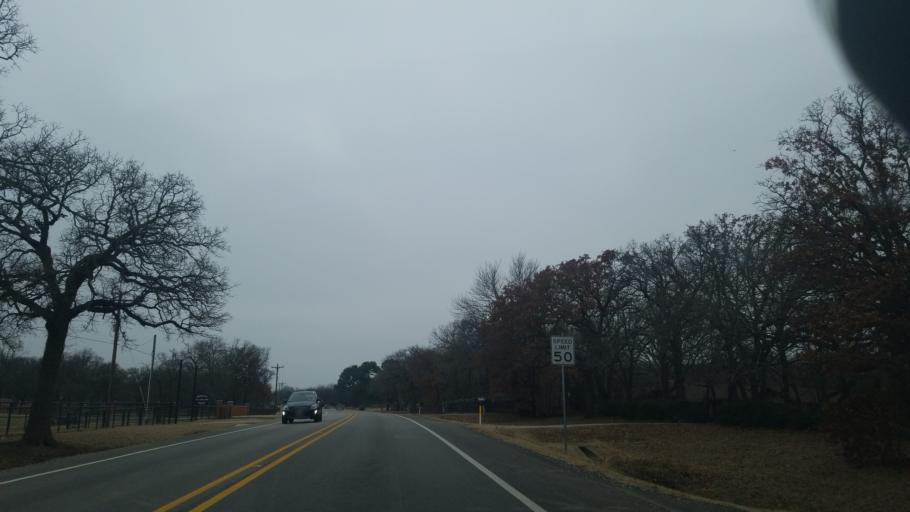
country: US
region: Texas
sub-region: Denton County
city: Argyle
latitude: 33.1430
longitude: -97.1482
